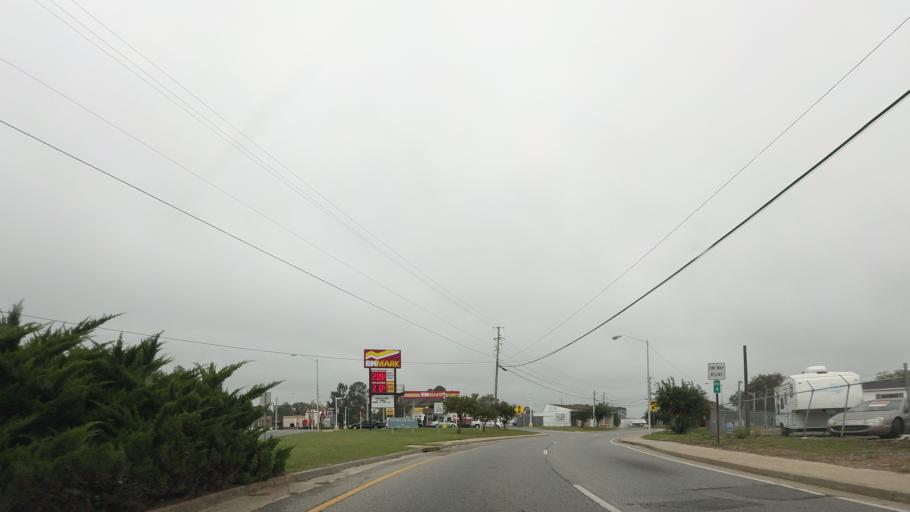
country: US
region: Georgia
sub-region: Ben Hill County
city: Fitzgerald
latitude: 31.7046
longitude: -83.2524
